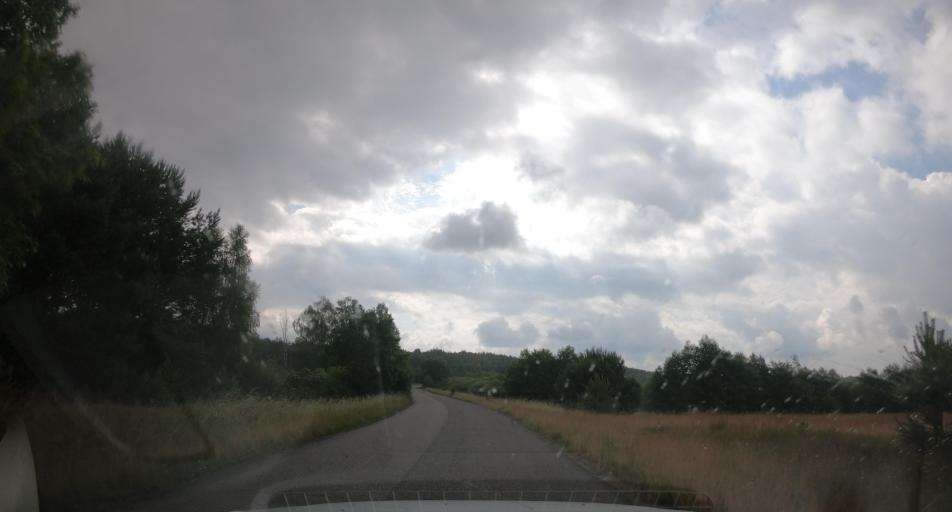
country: PL
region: West Pomeranian Voivodeship
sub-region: Powiat stargardzki
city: Insko
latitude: 53.3780
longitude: 15.6022
